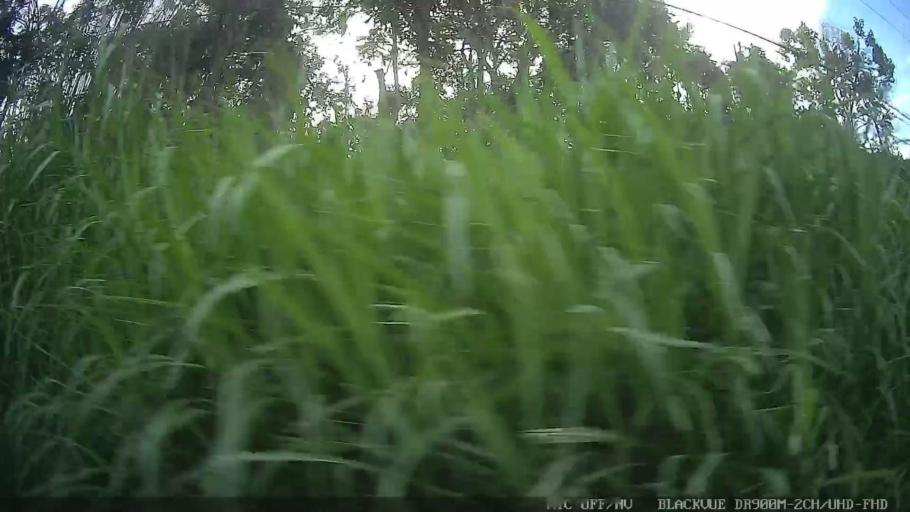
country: BR
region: Sao Paulo
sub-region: Mogi das Cruzes
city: Mogi das Cruzes
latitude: -23.5308
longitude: -46.1596
